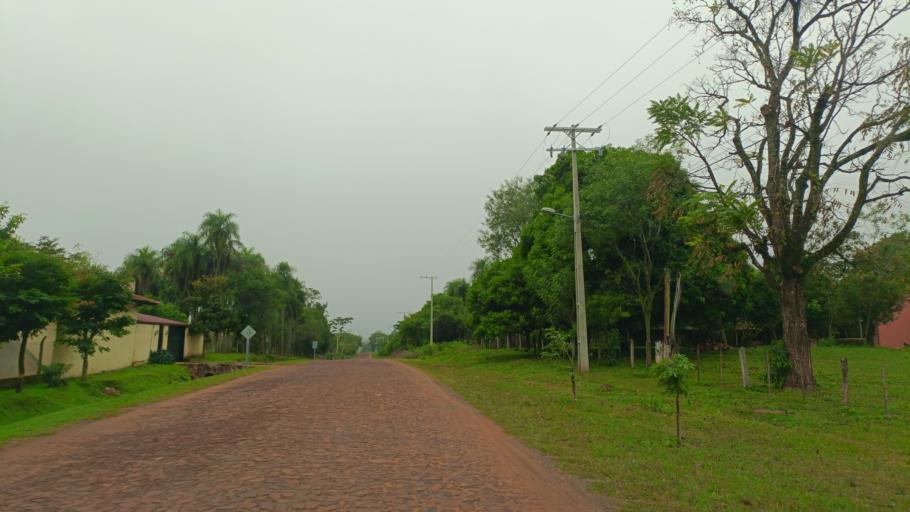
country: PY
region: Misiones
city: Santa Maria
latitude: -26.8621
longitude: -57.0210
